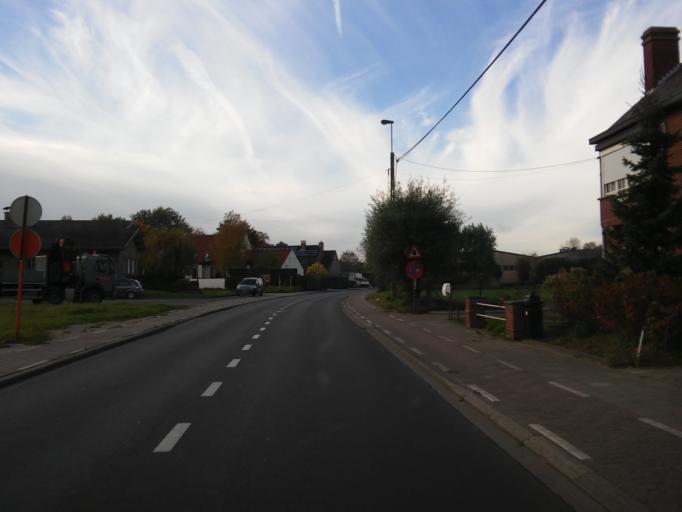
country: BE
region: Flanders
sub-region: Provincie Oost-Vlaanderen
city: Buggenhout
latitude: 51.0211
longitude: 4.1953
